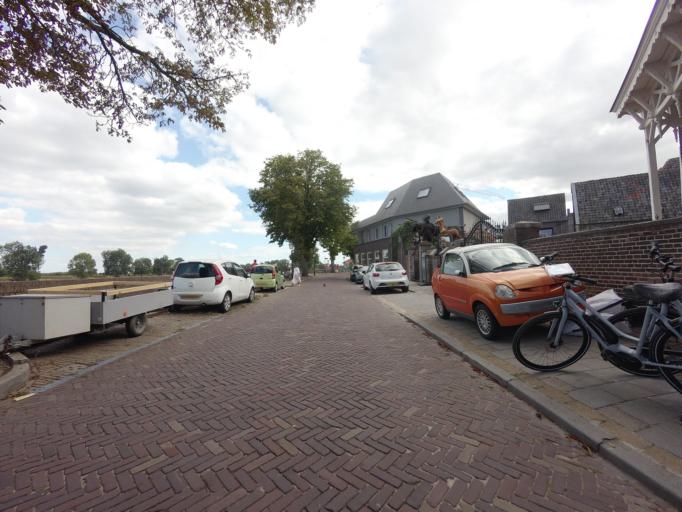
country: NL
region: North Brabant
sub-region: Gemeente Grave
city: Grave
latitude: 51.7603
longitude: 5.7419
